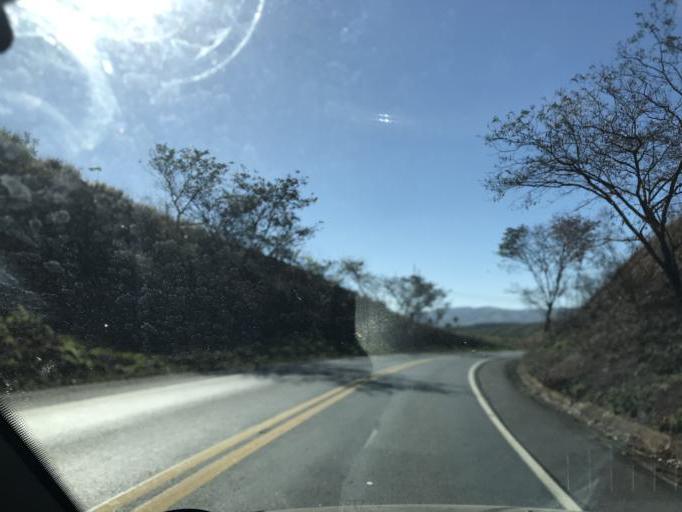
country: BR
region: Minas Gerais
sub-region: Bambui
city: Bambui
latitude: -19.8456
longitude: -45.9996
